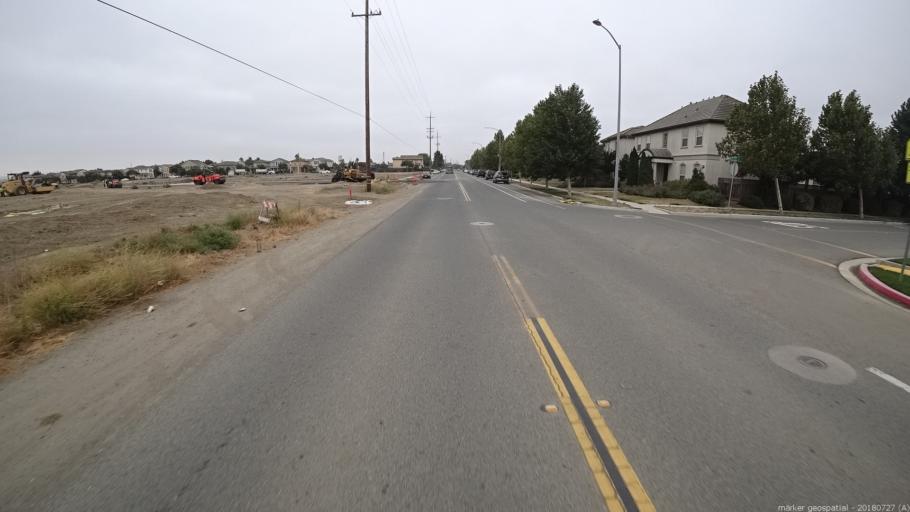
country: US
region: California
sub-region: Monterey County
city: King City
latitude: 36.2215
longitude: -121.1334
